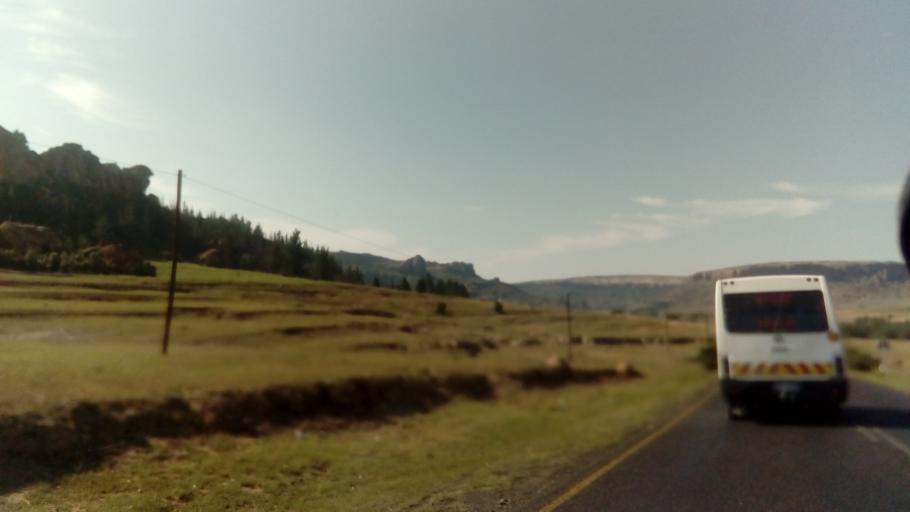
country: LS
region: Berea
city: Teyateyaneng
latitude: -29.1557
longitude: 27.6568
